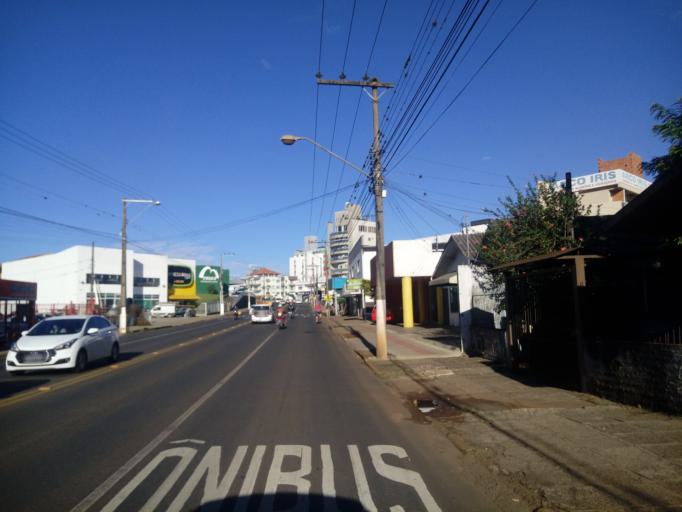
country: BR
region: Santa Catarina
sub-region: Chapeco
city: Chapeco
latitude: -27.0933
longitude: -52.6238
